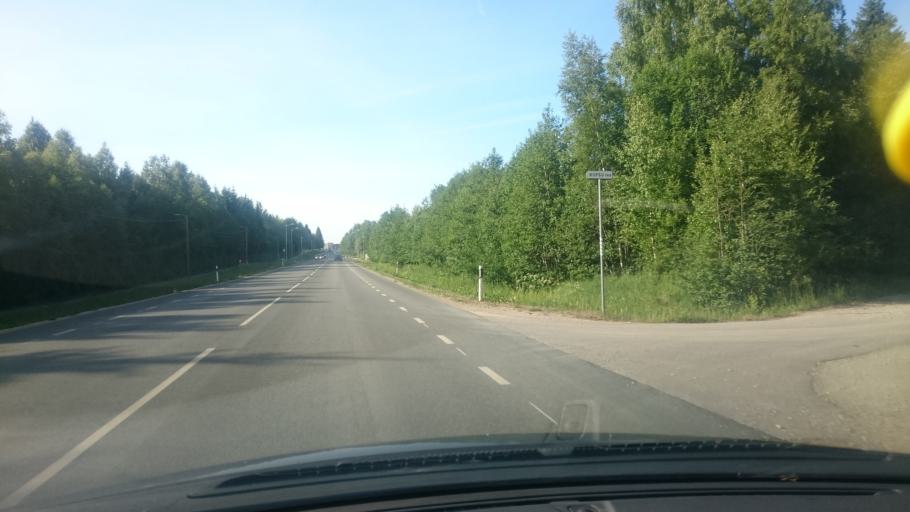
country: EE
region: Harju
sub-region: Saku vald
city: Saku
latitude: 59.2795
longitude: 24.6655
